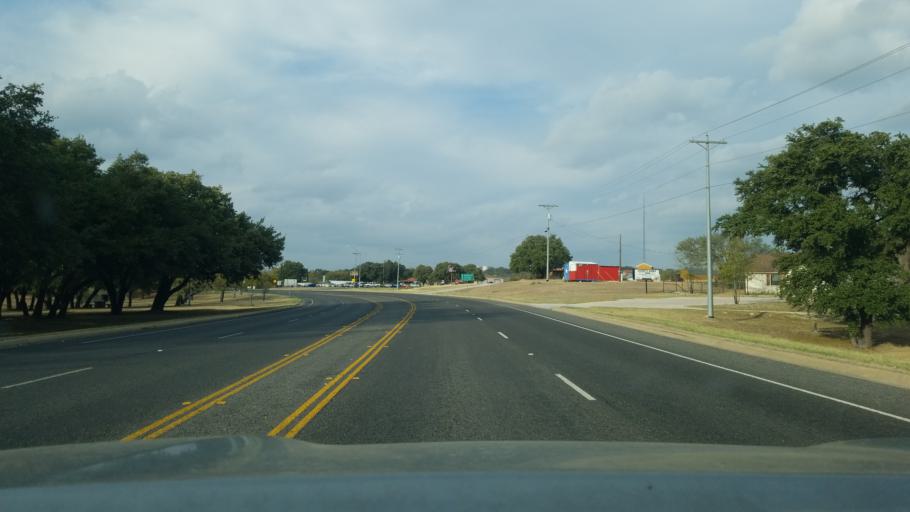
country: US
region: Texas
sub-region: Mills County
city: Goldthwaite
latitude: 31.4443
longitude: -98.5675
